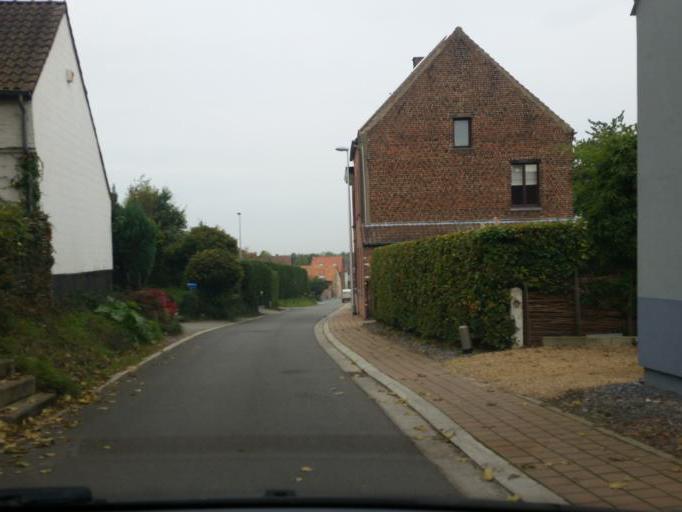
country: BE
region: Flanders
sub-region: Provincie Vlaams-Brabant
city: Halle
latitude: 50.7230
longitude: 4.2628
